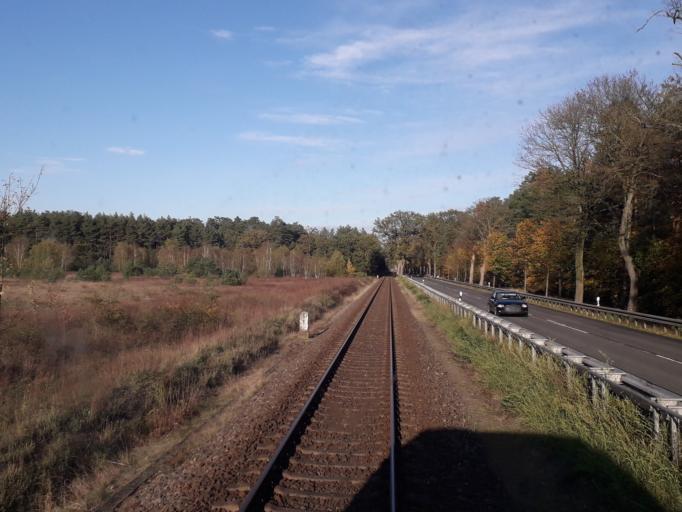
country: DE
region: Brandenburg
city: Weisen
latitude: 53.0330
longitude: 11.8020
